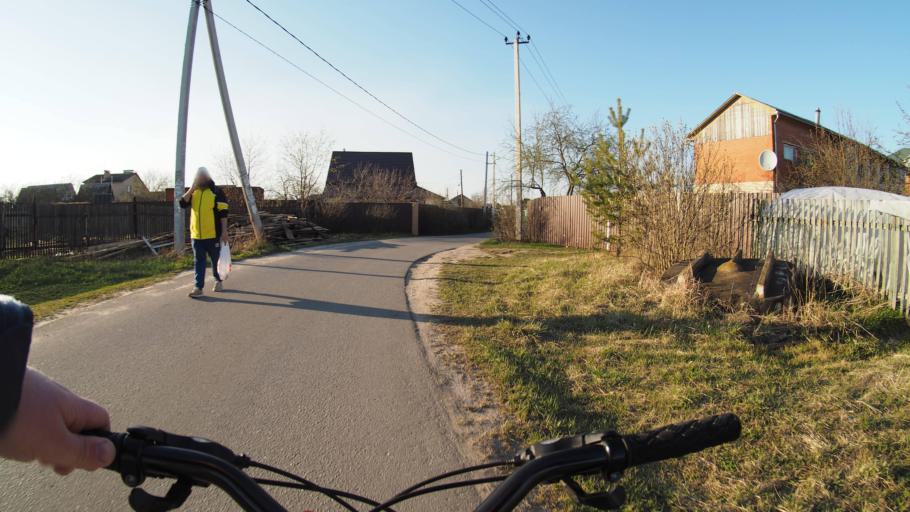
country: RU
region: Moskovskaya
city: Malyshevo
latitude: 55.4936
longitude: 38.3499
